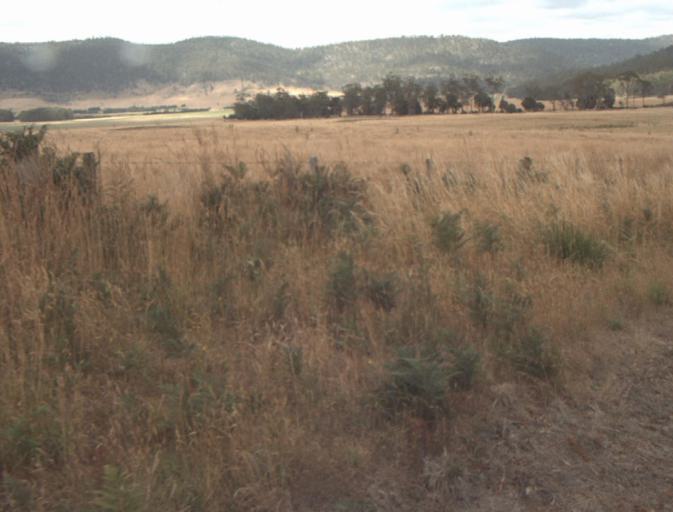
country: AU
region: Tasmania
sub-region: Northern Midlands
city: Evandale
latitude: -41.4603
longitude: 147.4569
